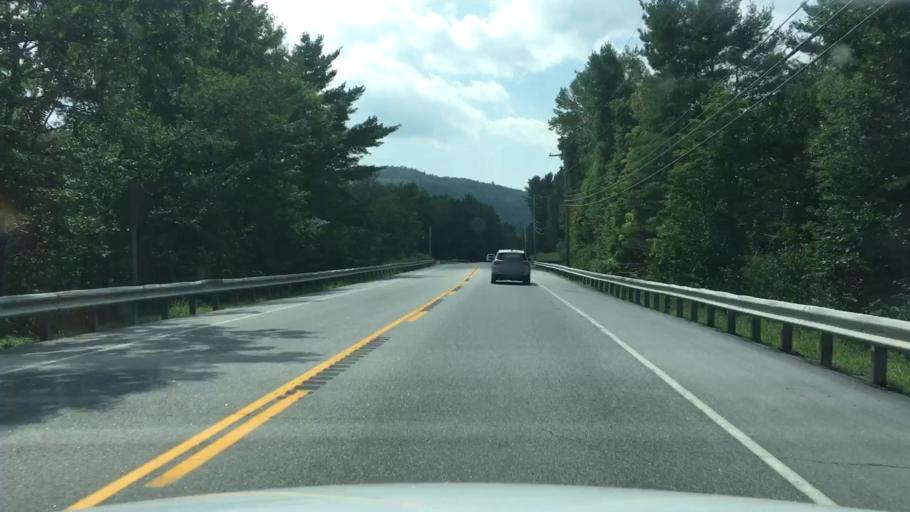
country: US
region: Maine
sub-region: Oxford County
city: Rumford
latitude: 44.5138
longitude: -70.5651
